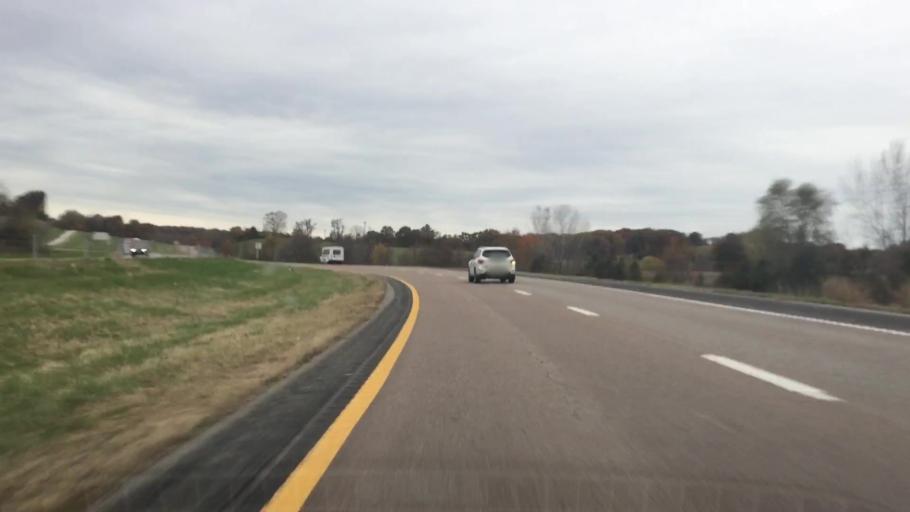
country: US
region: Missouri
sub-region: Cole County
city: Jefferson City
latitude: 38.6505
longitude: -92.2047
